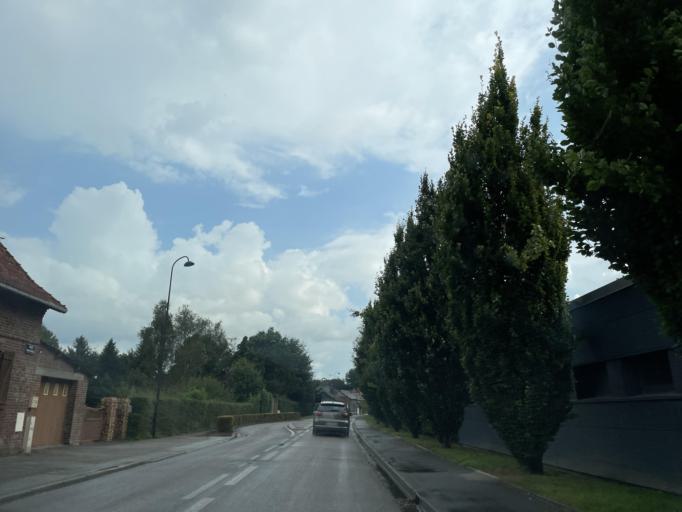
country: FR
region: Haute-Normandie
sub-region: Departement de la Seine-Maritime
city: Envermeu
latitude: 49.8917
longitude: 1.2746
